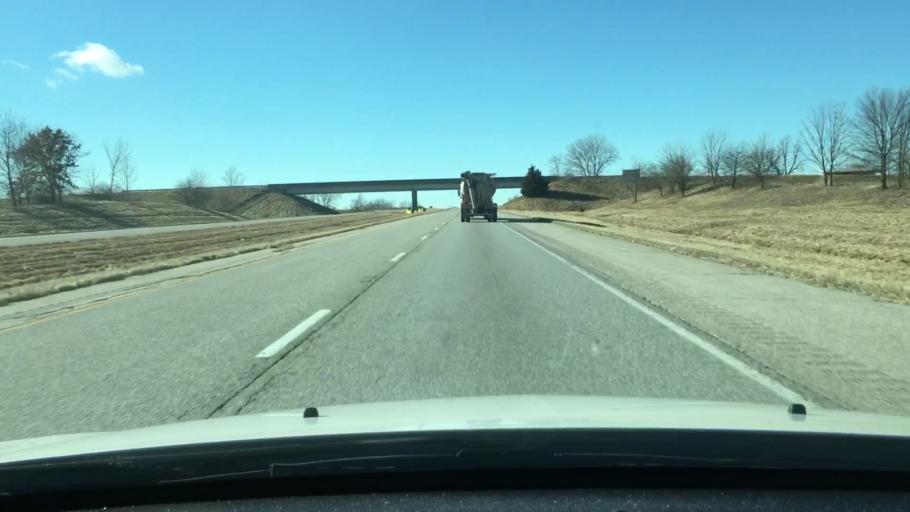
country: US
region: Illinois
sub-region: Pike County
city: Griggsville
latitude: 39.6784
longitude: -90.7014
